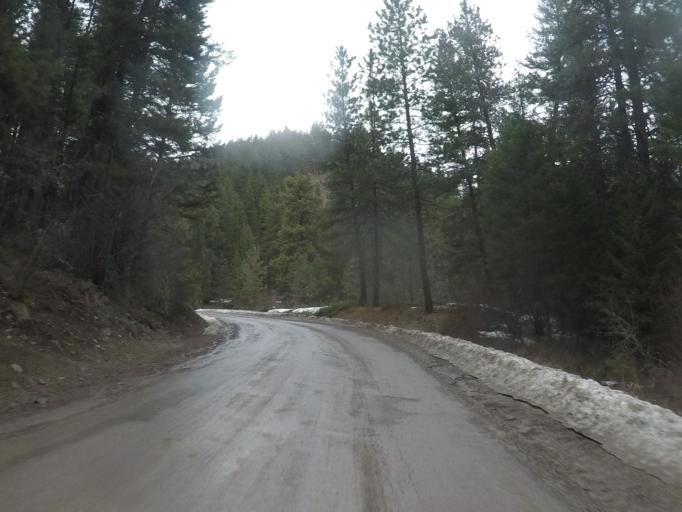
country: US
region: Montana
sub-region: Missoula County
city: East Missoula
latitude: 46.9236
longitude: -113.9613
